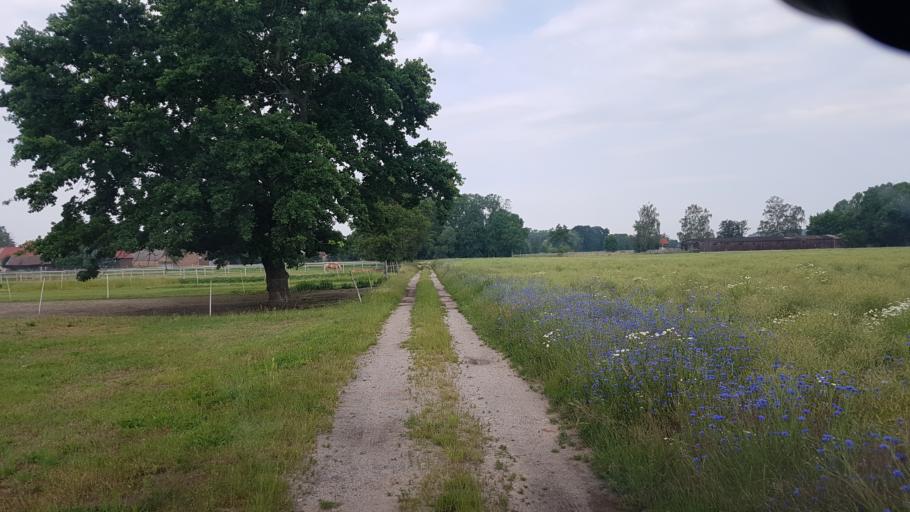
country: DE
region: Brandenburg
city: Schonewalde
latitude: 51.6812
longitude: 13.6052
